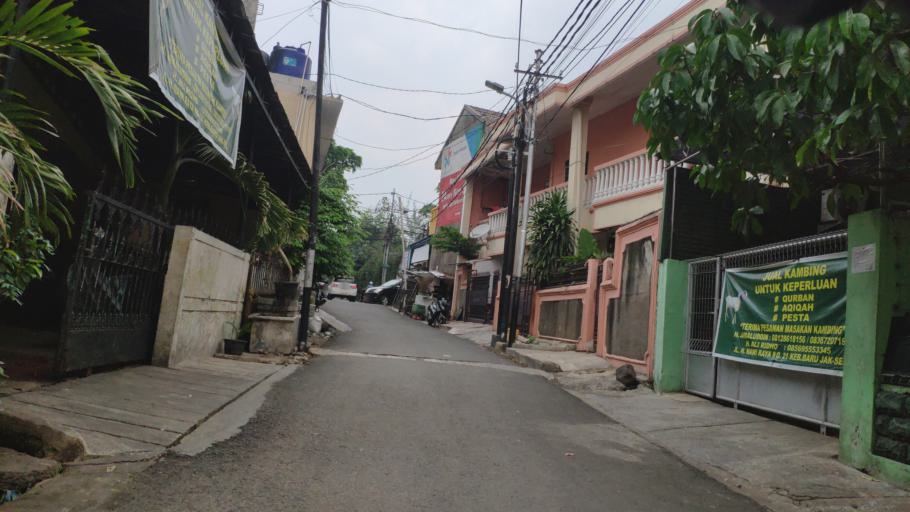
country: ID
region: Jakarta Raya
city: Jakarta
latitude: -6.2636
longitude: 106.7923
